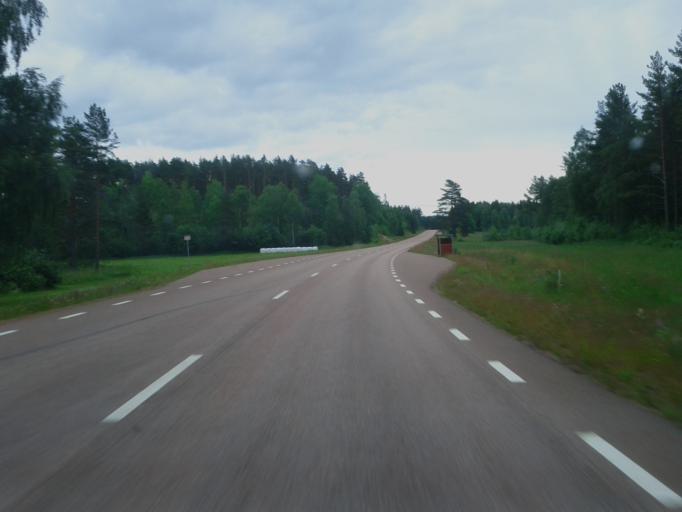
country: SE
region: Dalarna
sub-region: Alvdalens Kommun
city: AElvdalen
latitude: 61.2705
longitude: 13.9980
